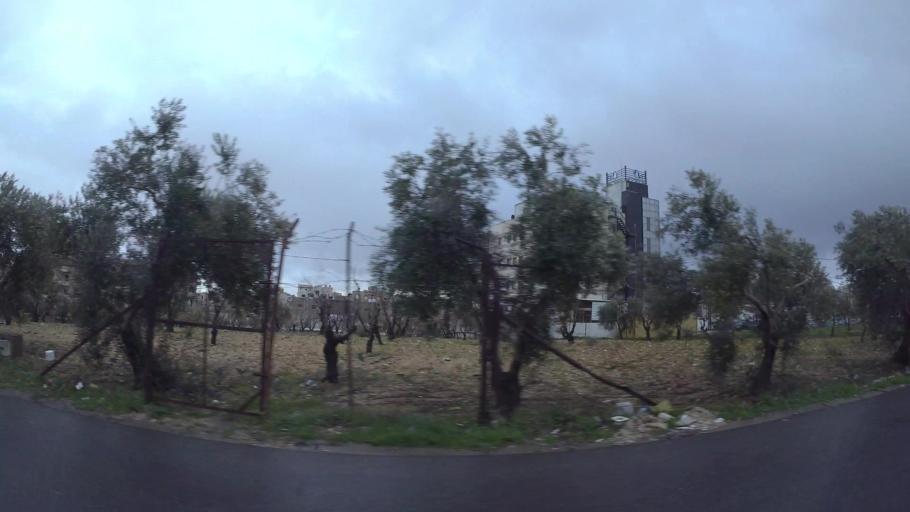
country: JO
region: Amman
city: Al Jubayhah
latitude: 32.0300
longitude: 35.8610
